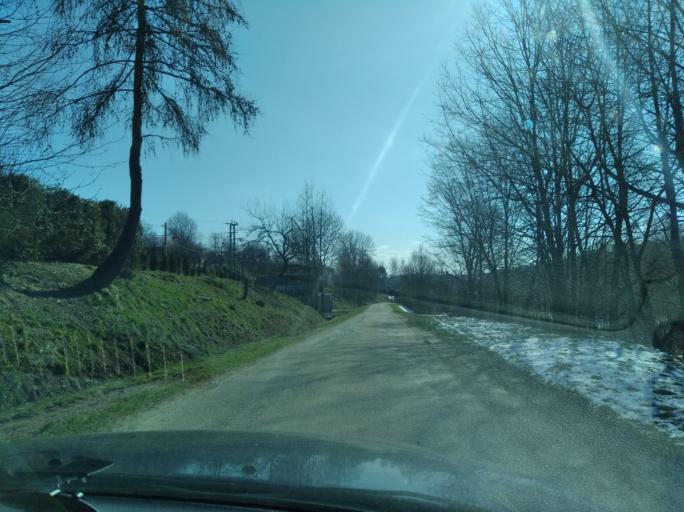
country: PL
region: Subcarpathian Voivodeship
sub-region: Powiat strzyzowski
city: Gwoznica Gorna
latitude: 49.8203
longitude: 22.0151
